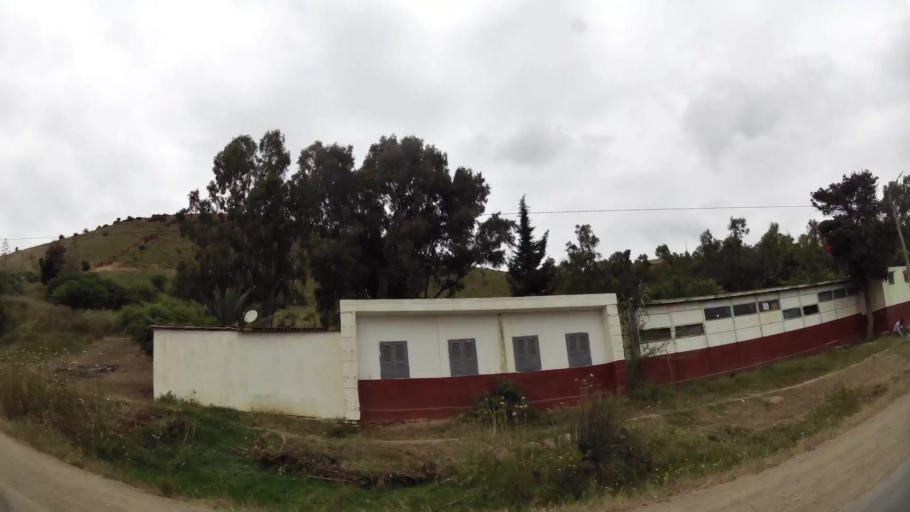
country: MA
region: Rabat-Sale-Zemmour-Zaer
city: Sale
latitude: 34.0044
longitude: -6.7778
